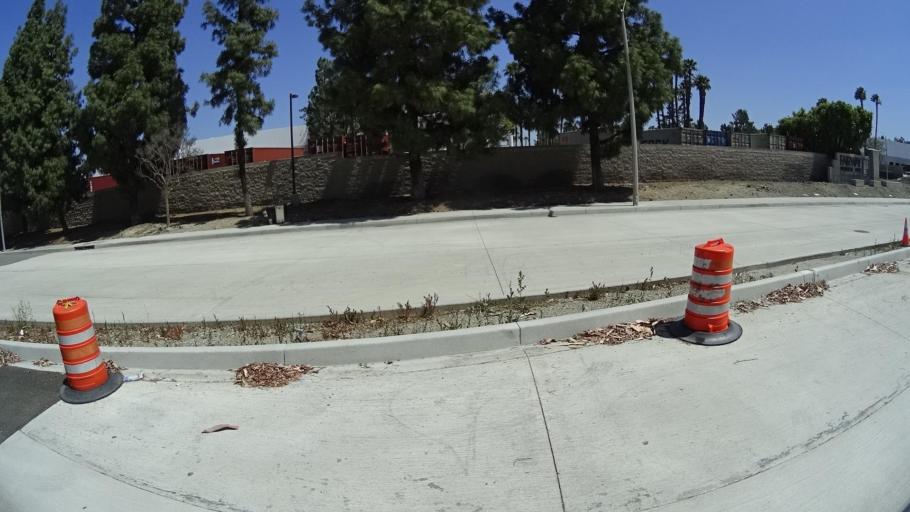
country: US
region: California
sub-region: Los Angeles County
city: Walnut
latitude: 33.9999
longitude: -117.8716
